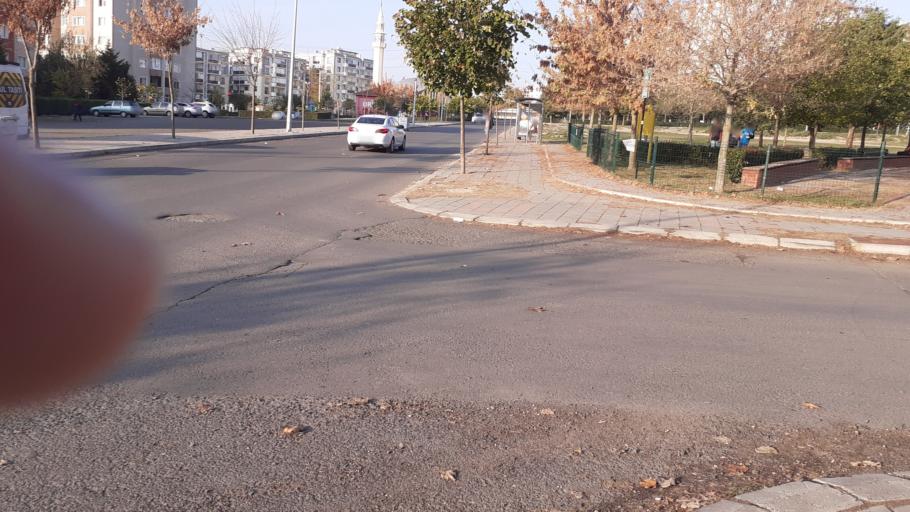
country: TR
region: Tekirdag
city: Corlu
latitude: 41.1457
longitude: 27.8272
